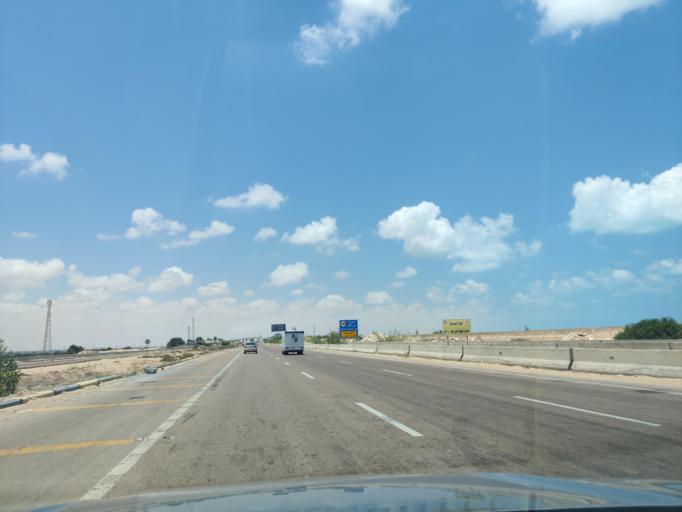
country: EG
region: Muhafazat Matruh
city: Al `Alamayn
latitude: 30.8126
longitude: 29.0753
